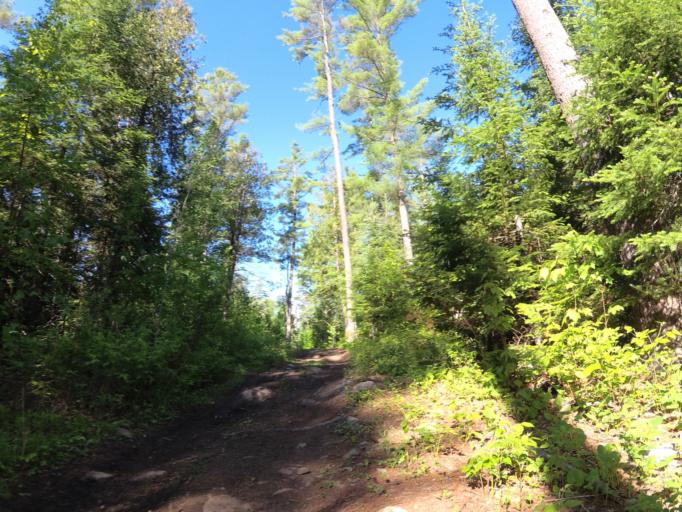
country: CA
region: Ontario
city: Renfrew
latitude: 45.1201
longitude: -77.0278
